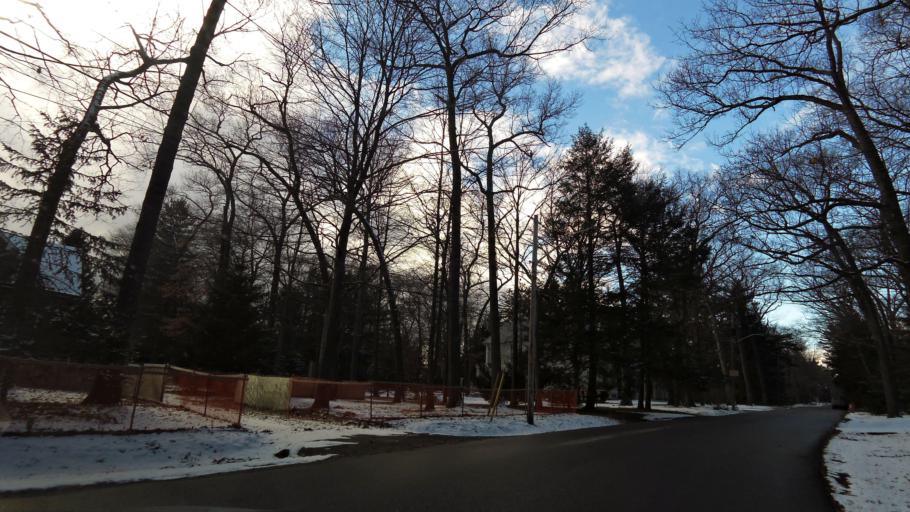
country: CA
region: Ontario
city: Mississauga
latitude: 43.5650
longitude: -79.6069
